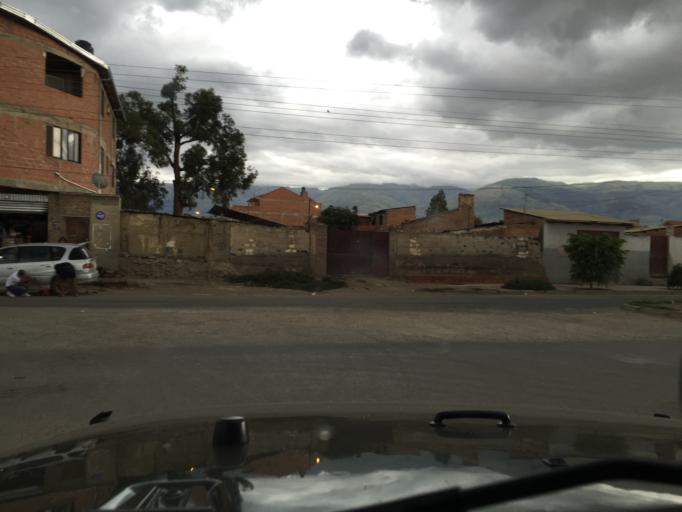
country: BO
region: Cochabamba
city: Cochabamba
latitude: -17.3973
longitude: -66.2123
